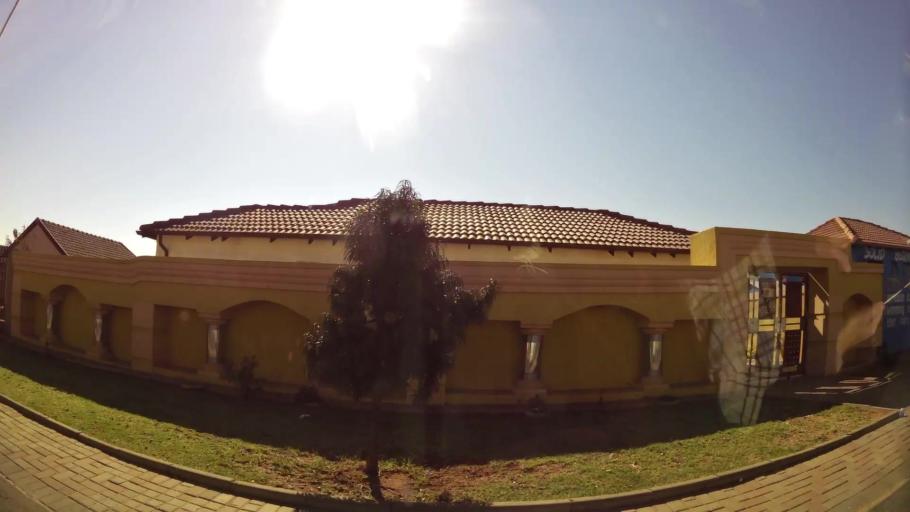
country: ZA
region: Gauteng
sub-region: Ekurhuleni Metropolitan Municipality
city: Tembisa
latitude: -26.0412
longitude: 28.2052
